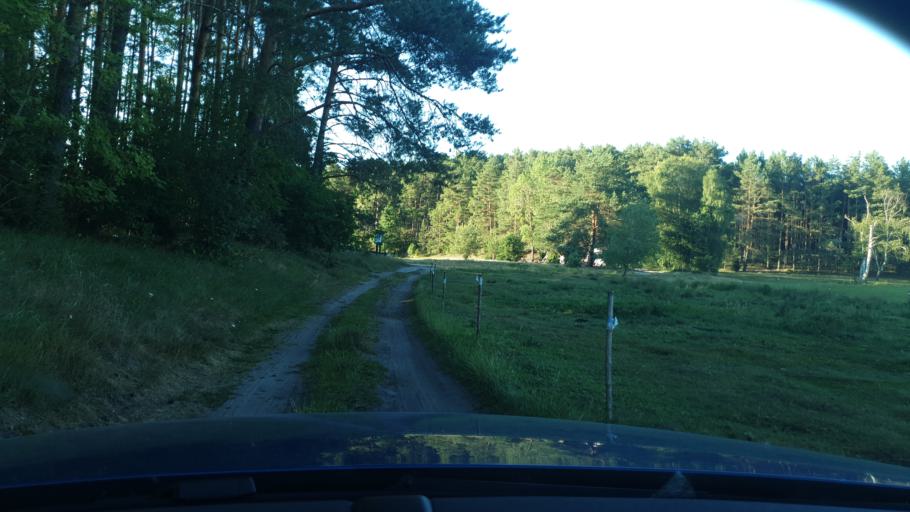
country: PL
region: Pomeranian Voivodeship
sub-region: Powiat bytowski
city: Lipnica
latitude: 53.8888
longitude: 17.4265
